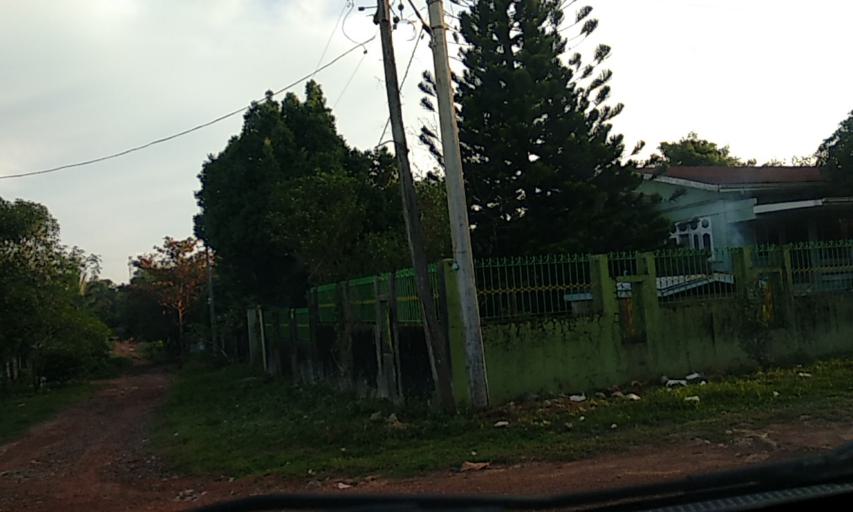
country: MM
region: Mon
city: Mawlamyine
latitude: 16.4580
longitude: 97.6517
